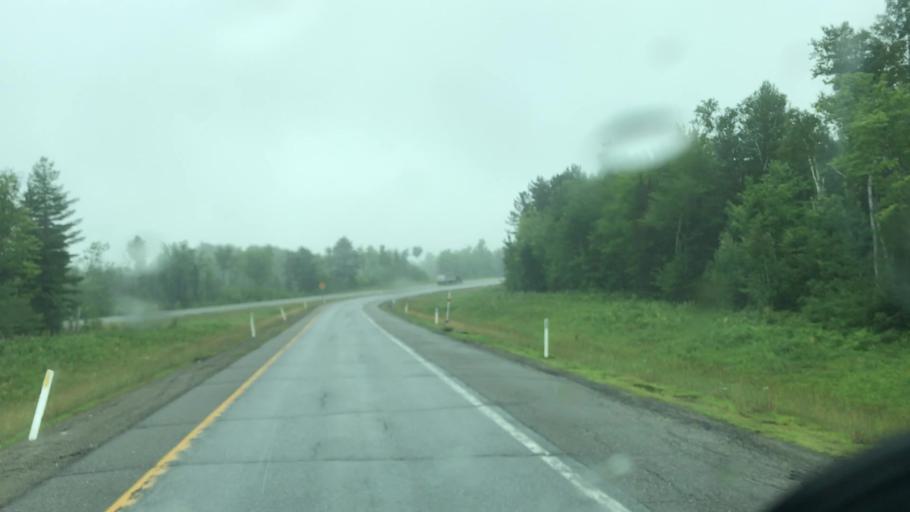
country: US
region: Maine
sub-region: Penobscot County
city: Howland
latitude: 45.2349
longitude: -68.6788
